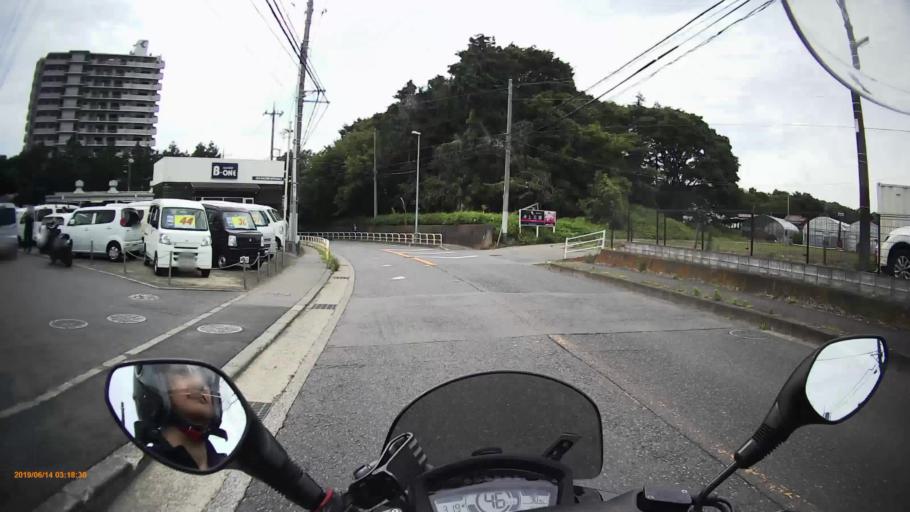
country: JP
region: Kanagawa
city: Minami-rinkan
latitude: 35.4193
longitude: 139.4554
